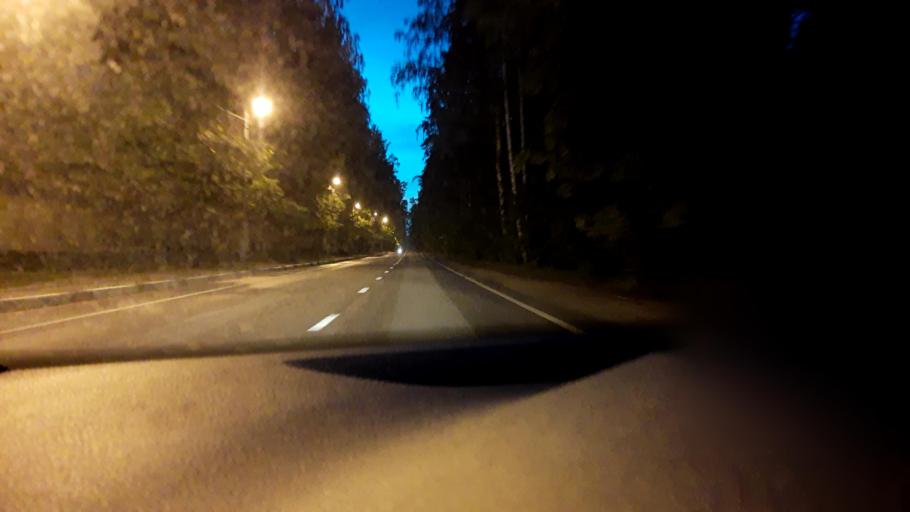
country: RU
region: Moskovskaya
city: Petrovo-Dal'neye
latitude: 55.7916
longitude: 37.2049
